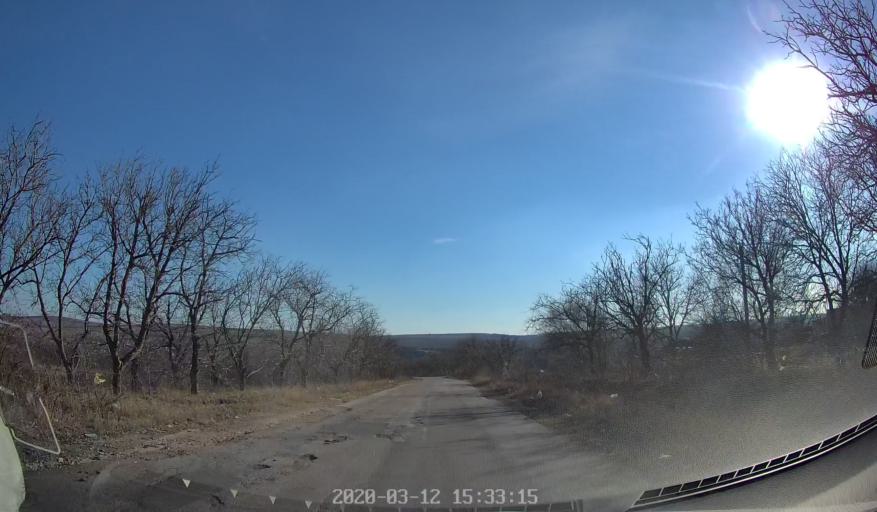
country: MD
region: Chisinau
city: Ciorescu
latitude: 47.1448
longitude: 28.9378
